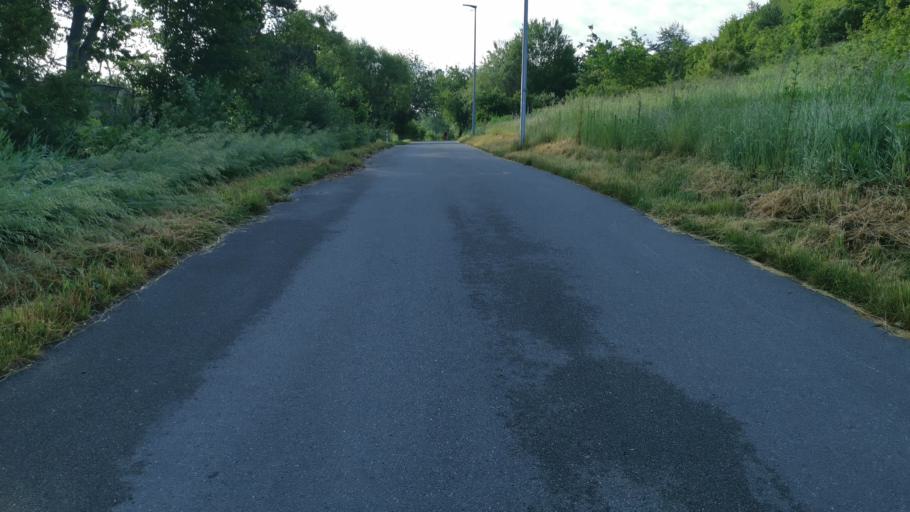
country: DE
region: Bavaria
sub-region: Regierungsbezirk Mittelfranken
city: Grossreuth bei Schweinau
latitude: 49.4227
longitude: 11.0472
